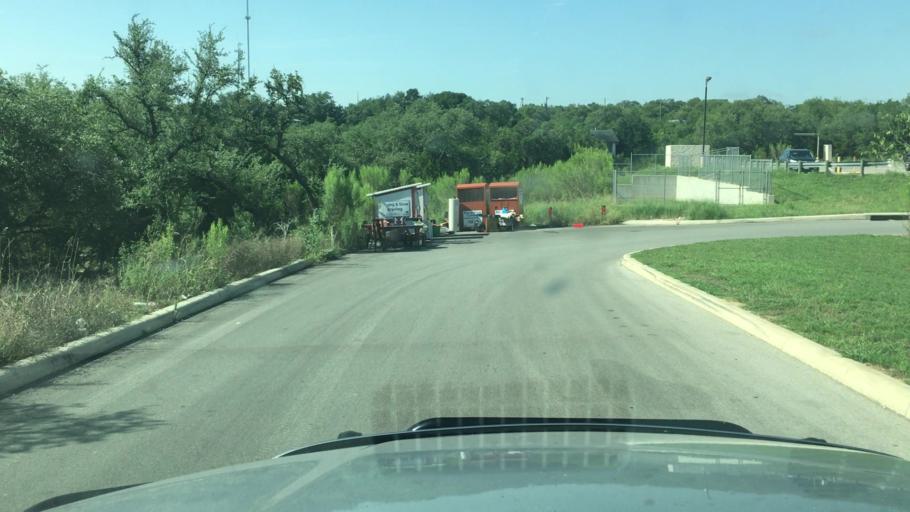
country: US
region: Texas
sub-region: Bexar County
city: Timberwood Park
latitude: 29.6921
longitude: -98.4510
